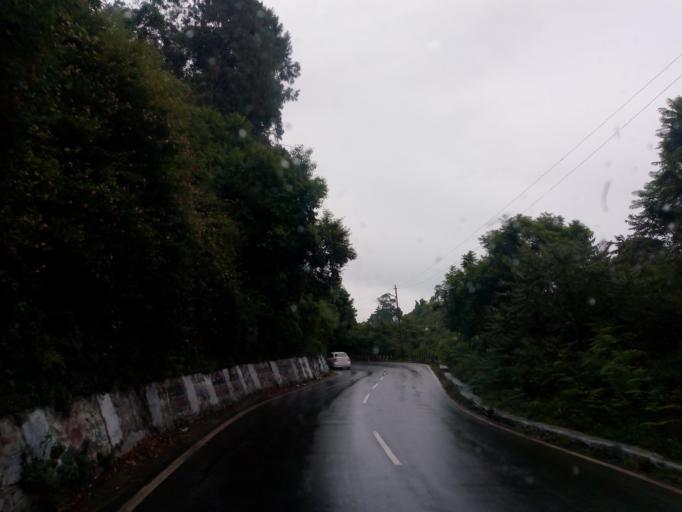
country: IN
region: Tamil Nadu
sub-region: Nilgiri
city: Wellington
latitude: 11.3467
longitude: 76.7885
